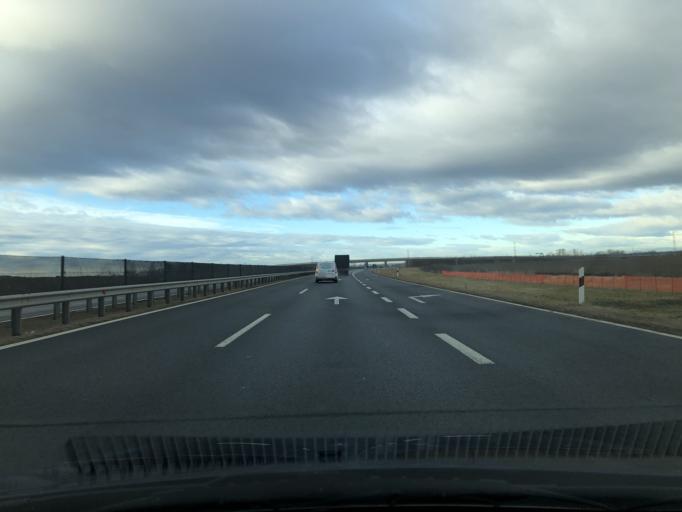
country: HU
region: Vas
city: Vep
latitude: 47.2575
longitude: 16.7251
